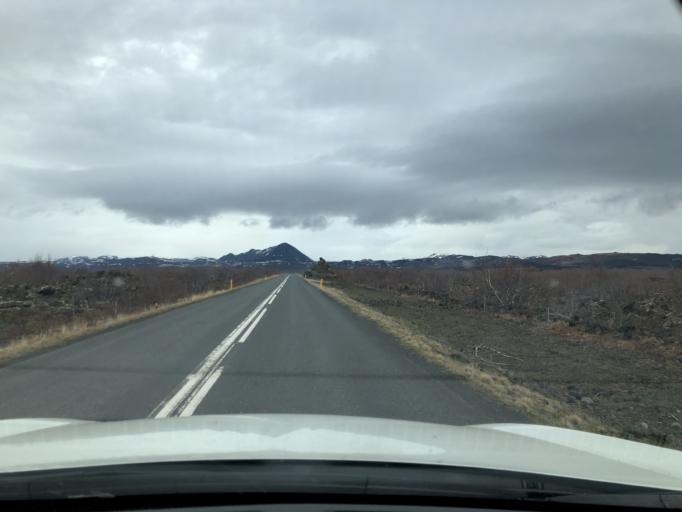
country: IS
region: Northeast
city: Laugar
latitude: 65.6029
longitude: -16.9247
